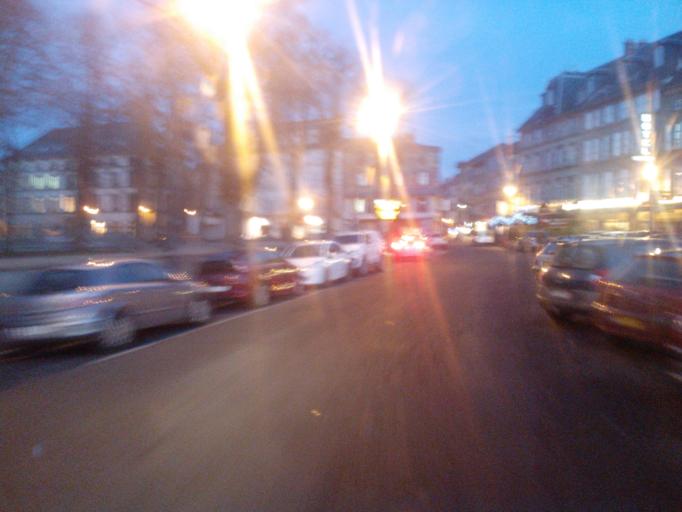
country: FR
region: Auvergne
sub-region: Departement du Cantal
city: Saint-Flour
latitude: 45.0330
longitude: 3.0883
